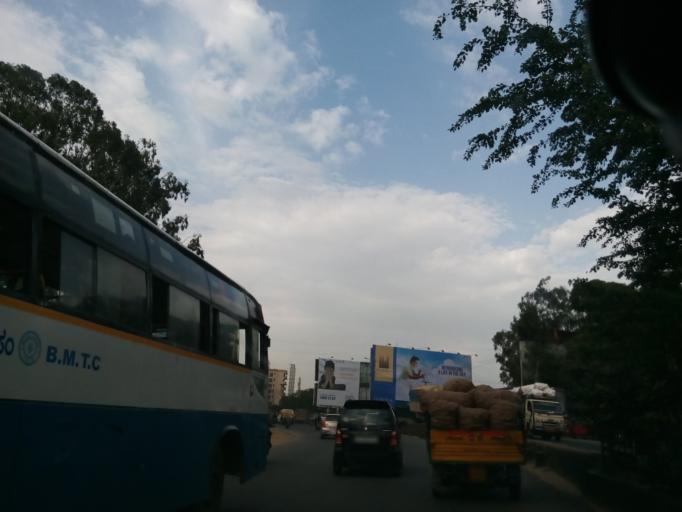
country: IN
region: Karnataka
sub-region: Bangalore Urban
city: Bangalore
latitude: 13.0154
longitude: 77.5548
